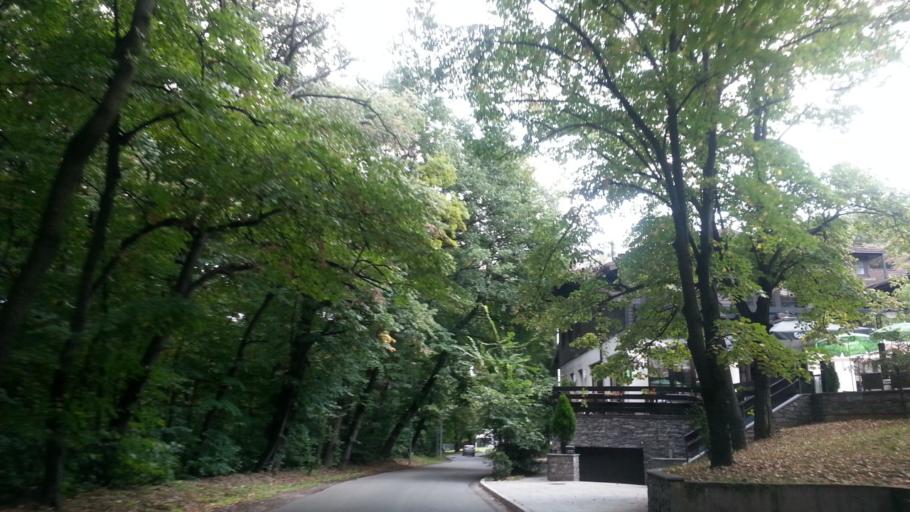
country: RS
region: Central Serbia
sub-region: Belgrade
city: Rakovica
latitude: 44.7626
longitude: 20.4331
